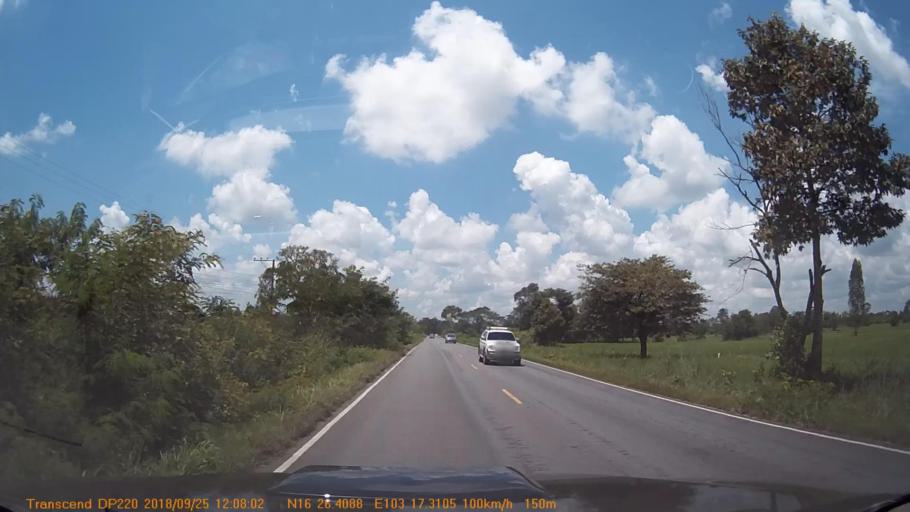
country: TH
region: Kalasin
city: Yang Talat
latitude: 16.4401
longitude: 103.2887
